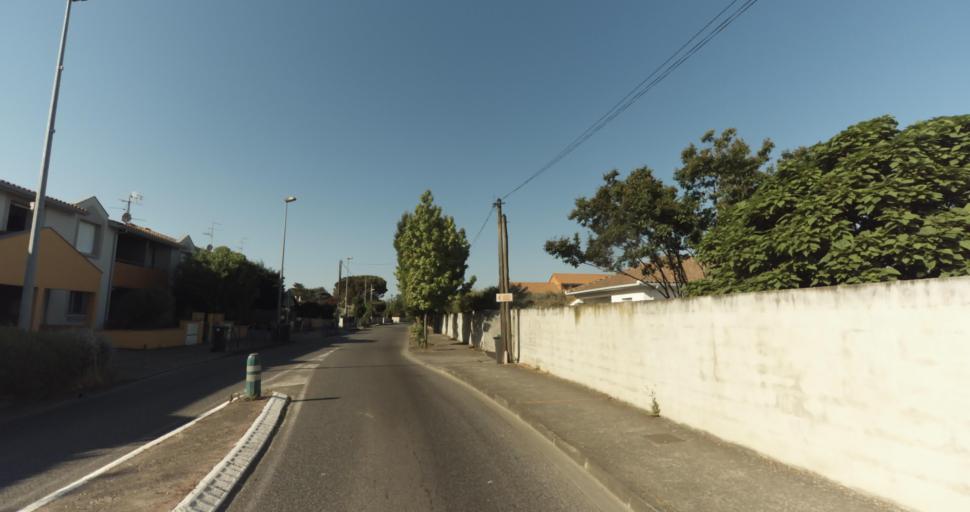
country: FR
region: Midi-Pyrenees
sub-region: Departement de la Haute-Garonne
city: La Salvetat-Saint-Gilles
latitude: 43.5752
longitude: 1.2720
